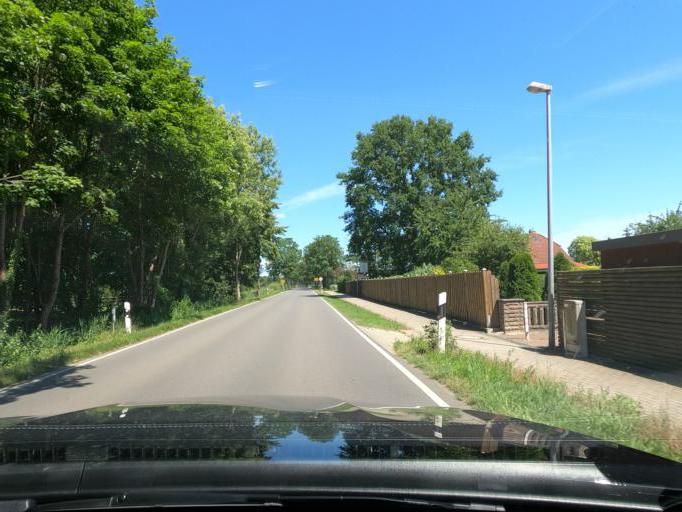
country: DE
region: Lower Saxony
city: Haenigsen
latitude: 52.4931
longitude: 10.1166
